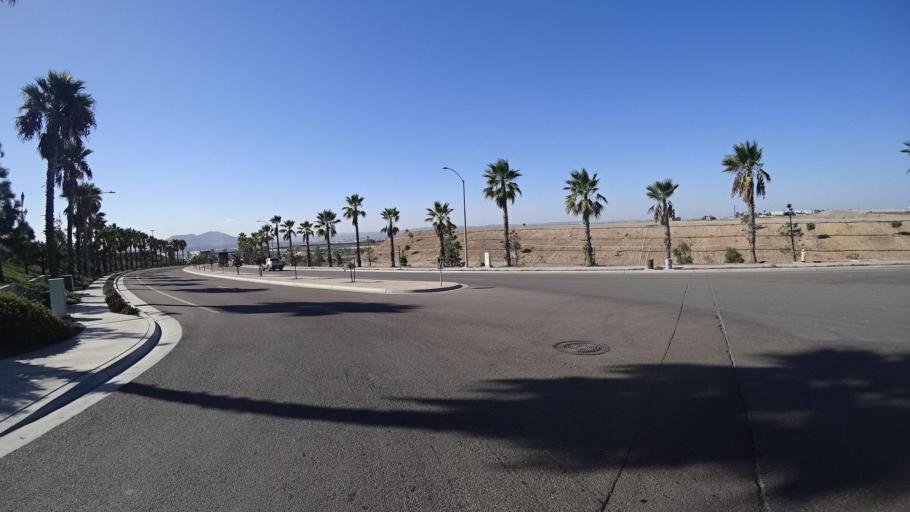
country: MX
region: Baja California
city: Tijuana
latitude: 32.5692
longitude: -116.9130
